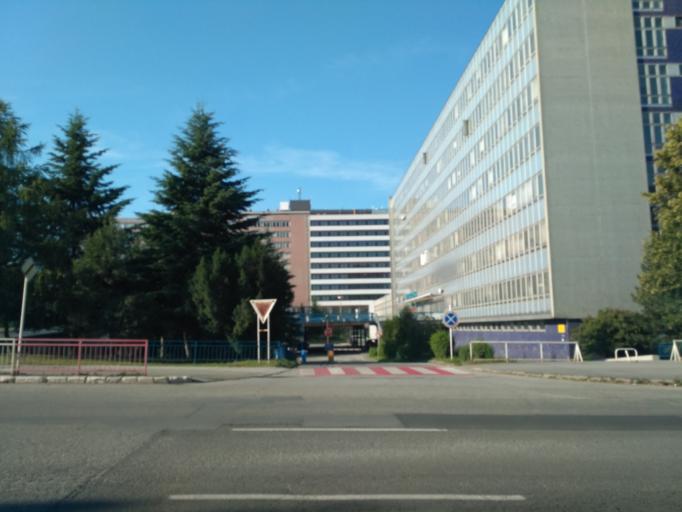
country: SK
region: Kosicky
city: Kosice
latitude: 48.7215
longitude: 21.2368
